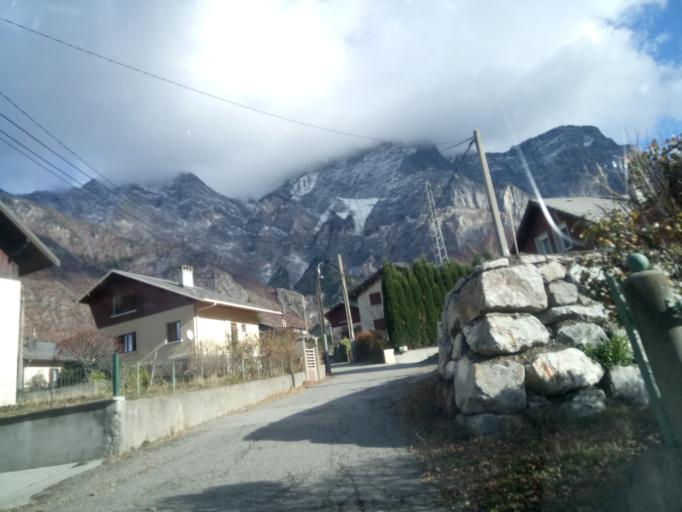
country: FR
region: Rhone-Alpes
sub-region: Departement de la Savoie
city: Villargondran
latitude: 45.2493
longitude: 6.4122
